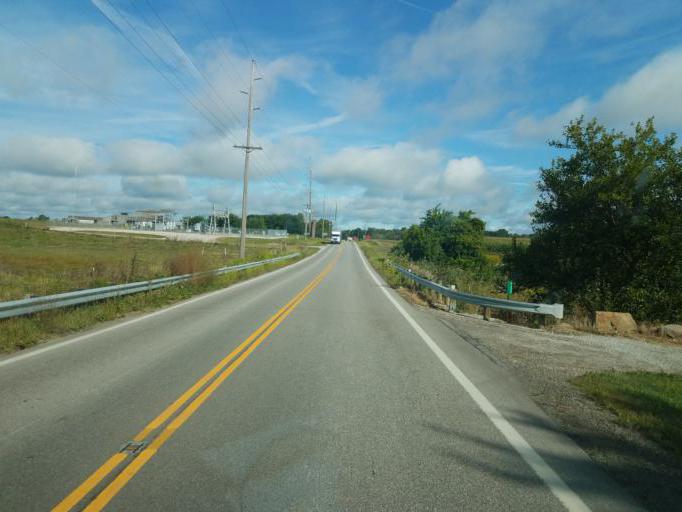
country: US
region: Ohio
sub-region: Wayne County
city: West Salem
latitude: 41.0172
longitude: -82.1207
